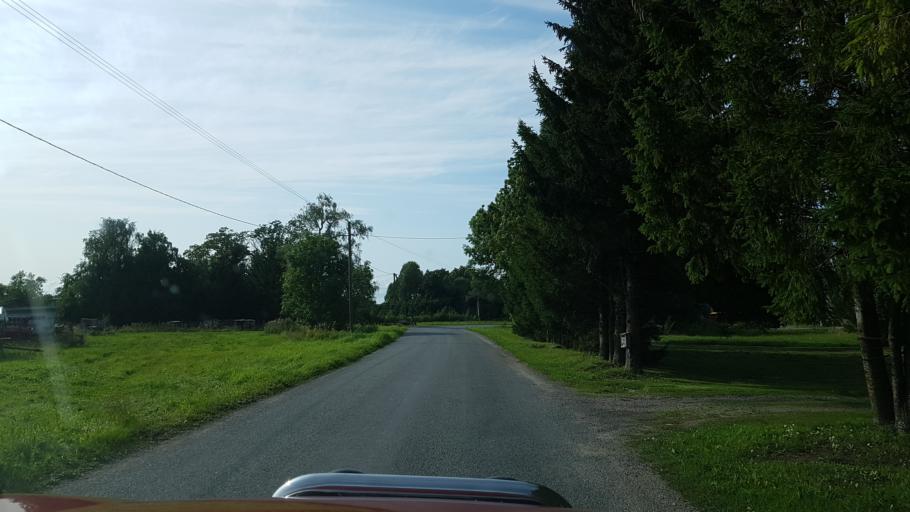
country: EE
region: Laeaene
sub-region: Lihula vald
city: Lihula
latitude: 58.4484
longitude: 23.9999
